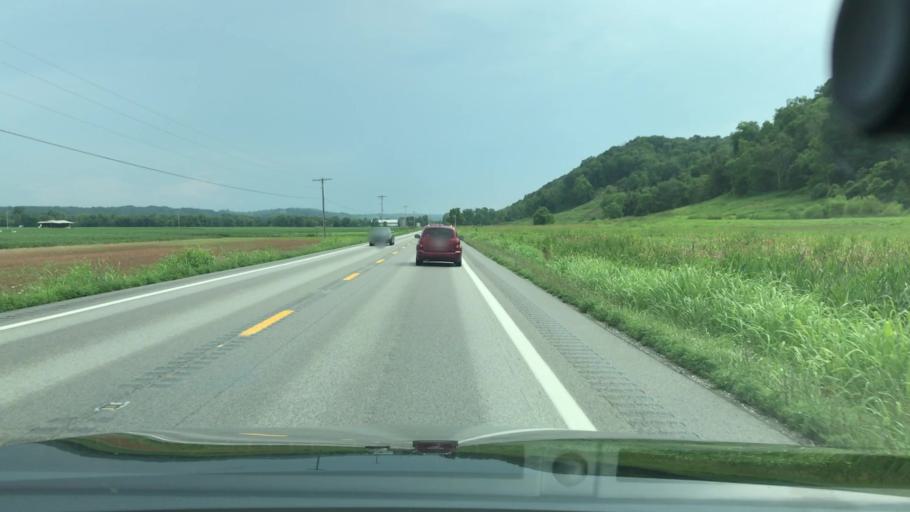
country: US
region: West Virginia
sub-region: Putnam County
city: Buffalo
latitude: 38.6676
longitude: -81.9673
